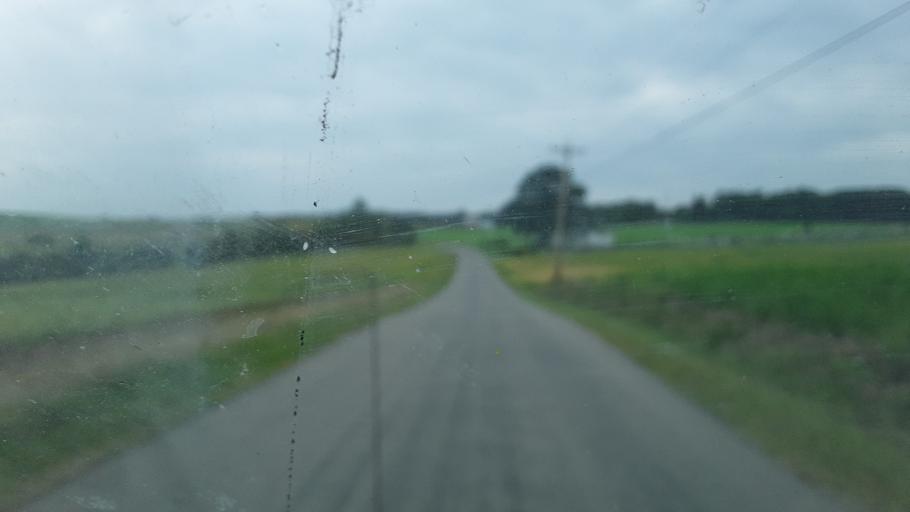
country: US
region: Pennsylvania
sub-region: Jefferson County
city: Punxsutawney
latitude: 40.9469
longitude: -79.1401
